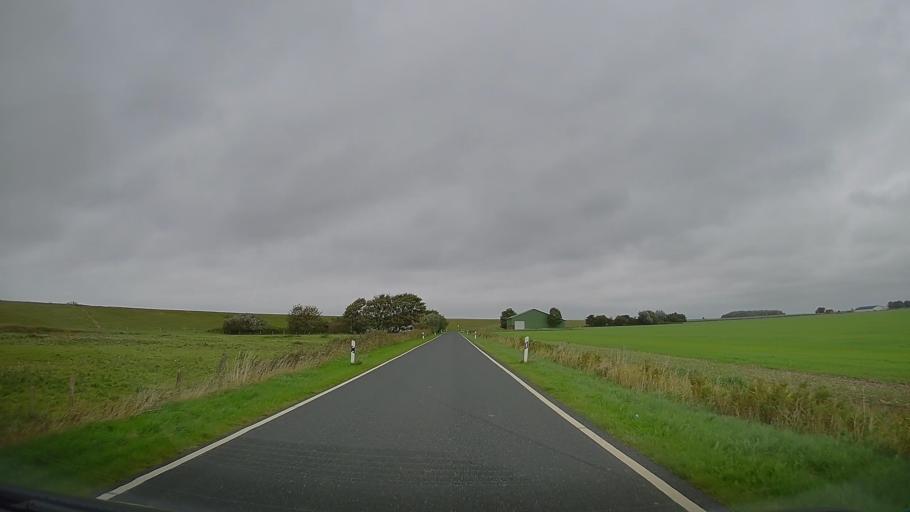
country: DE
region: Schleswig-Holstein
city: Friedrichskoog
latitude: 54.0254
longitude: 8.9174
